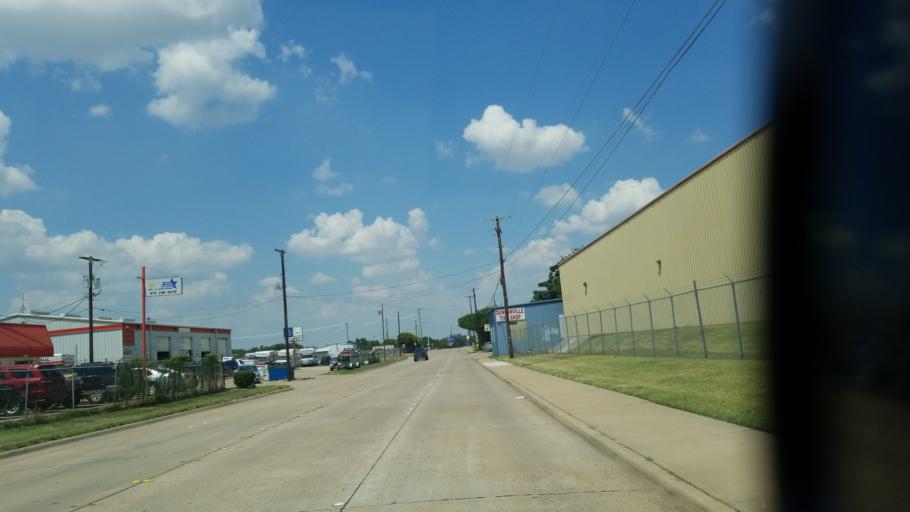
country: US
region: Texas
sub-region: Dallas County
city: Duncanville
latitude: 32.6721
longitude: -96.9044
